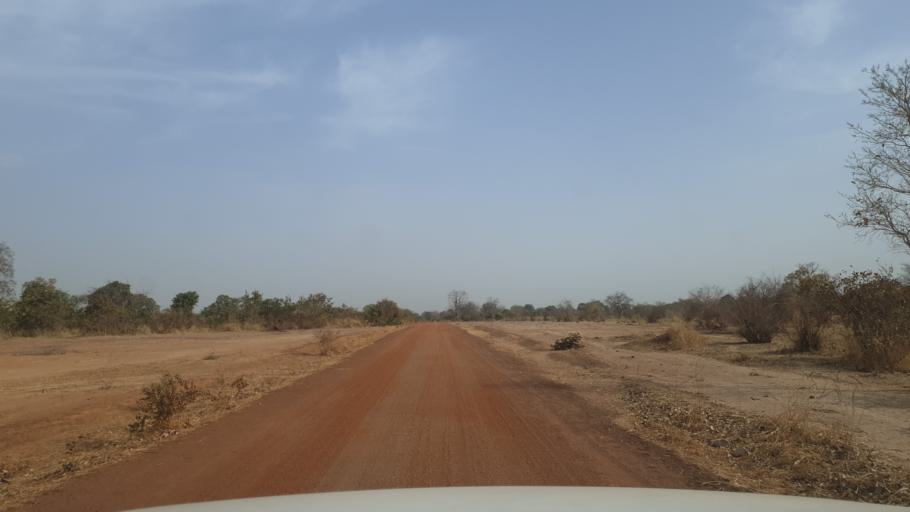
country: ML
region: Koulikoro
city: Kolokani
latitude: 13.3115
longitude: -8.2790
